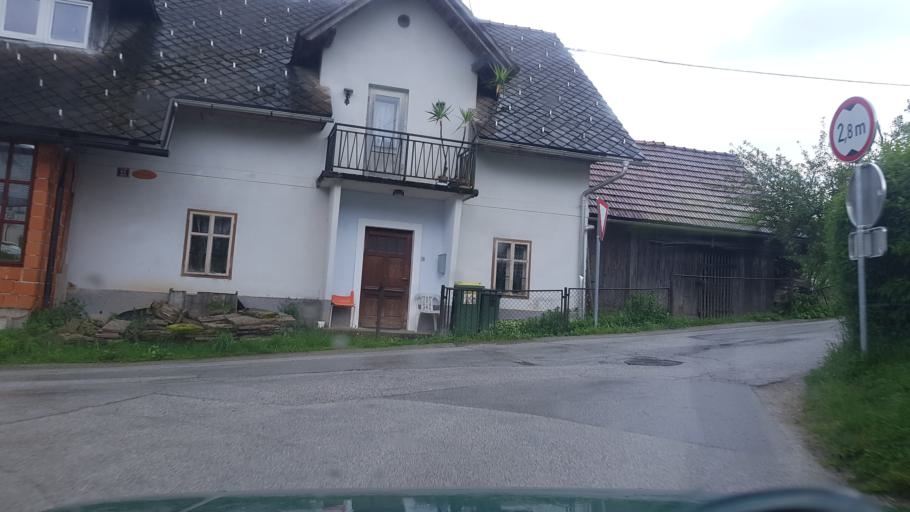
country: SI
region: Gorje
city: Zgornje Gorje
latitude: 46.3887
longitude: 14.0851
